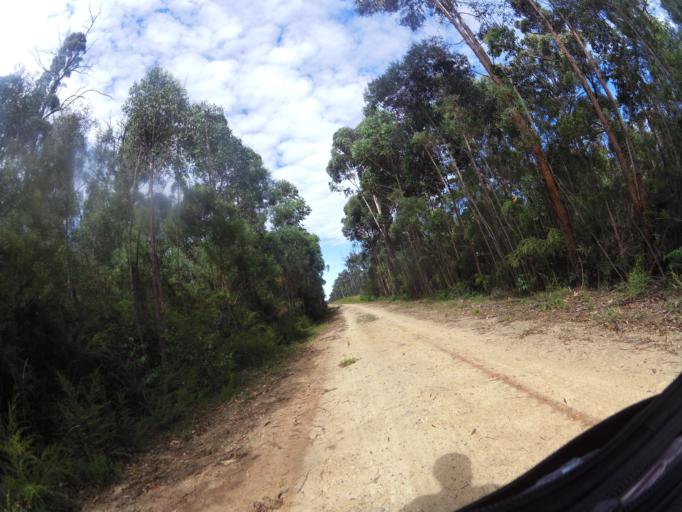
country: AU
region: Victoria
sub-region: East Gippsland
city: Lakes Entrance
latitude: -37.7454
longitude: 148.2423
